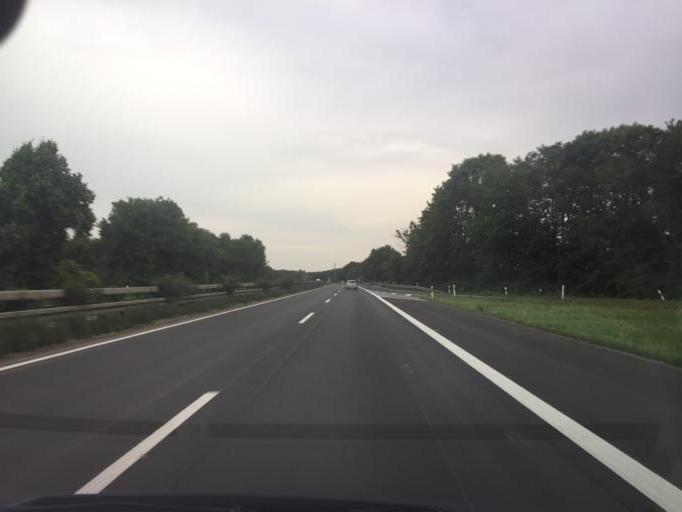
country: DE
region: North Rhine-Westphalia
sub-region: Regierungsbezirk Dusseldorf
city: Viersen
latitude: 51.2373
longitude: 6.3607
